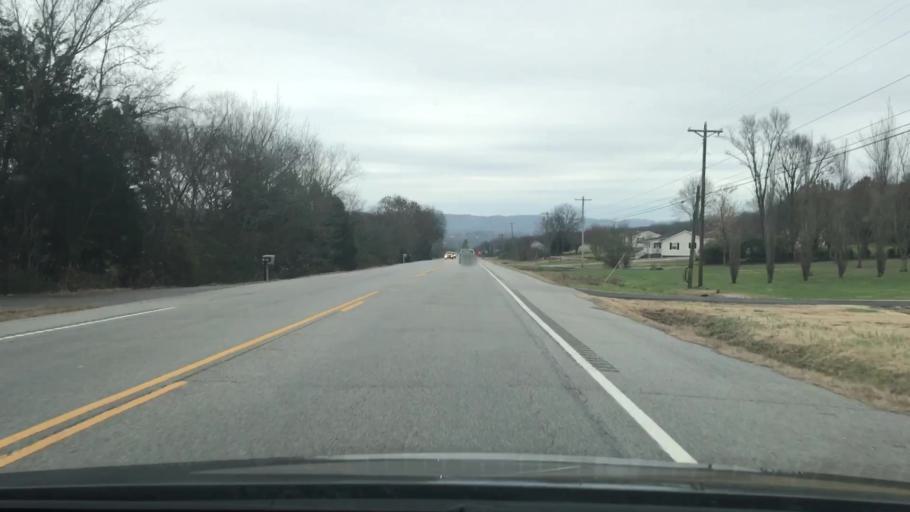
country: US
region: Tennessee
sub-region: Trousdale County
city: Hartsville
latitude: 36.3686
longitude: -86.0916
